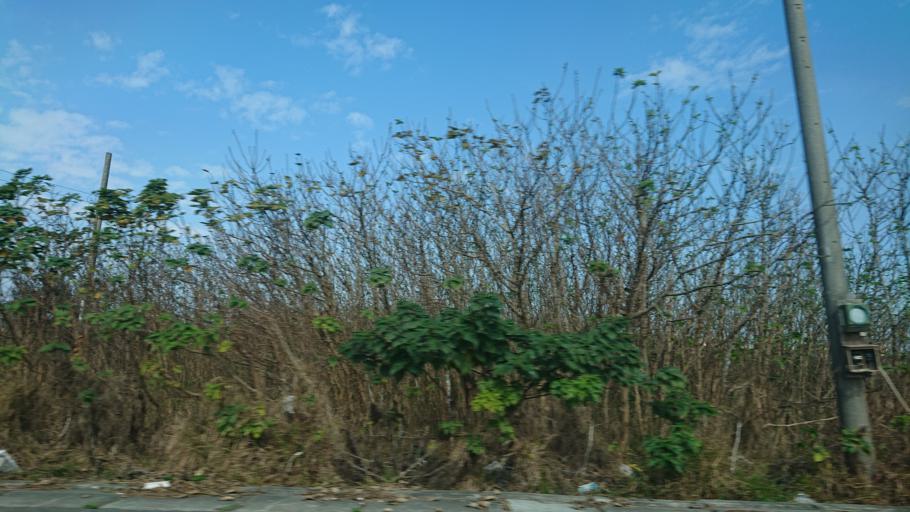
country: TW
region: Taiwan
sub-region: Changhua
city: Chang-hua
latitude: 23.9203
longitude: 120.3193
